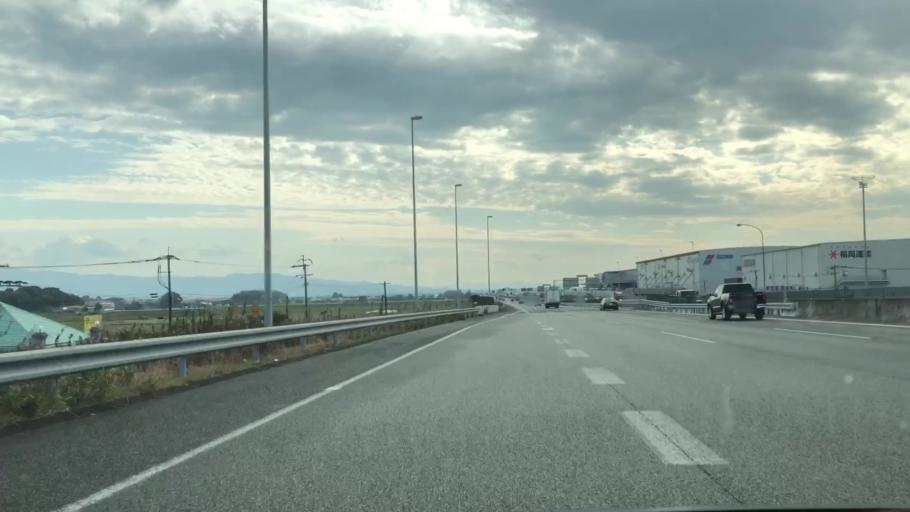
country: JP
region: Saga Prefecture
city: Tosu
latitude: 33.3929
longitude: 130.5384
